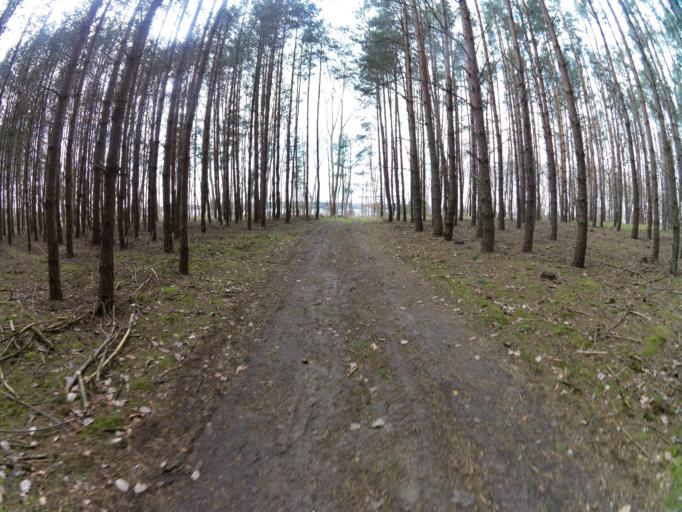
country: PL
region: West Pomeranian Voivodeship
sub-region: Powiat mysliborski
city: Mysliborz
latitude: 52.9589
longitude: 14.8757
